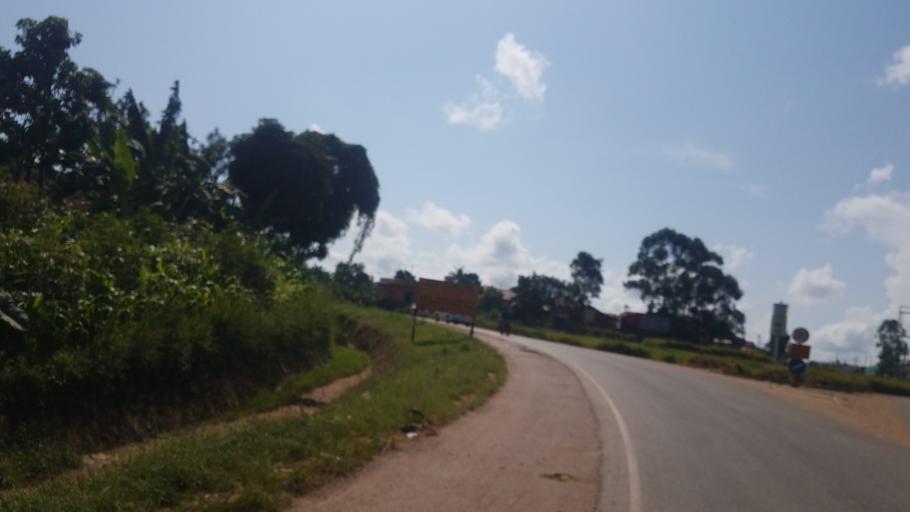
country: UG
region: Central Region
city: Masaka
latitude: -0.3366
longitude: 31.7191
